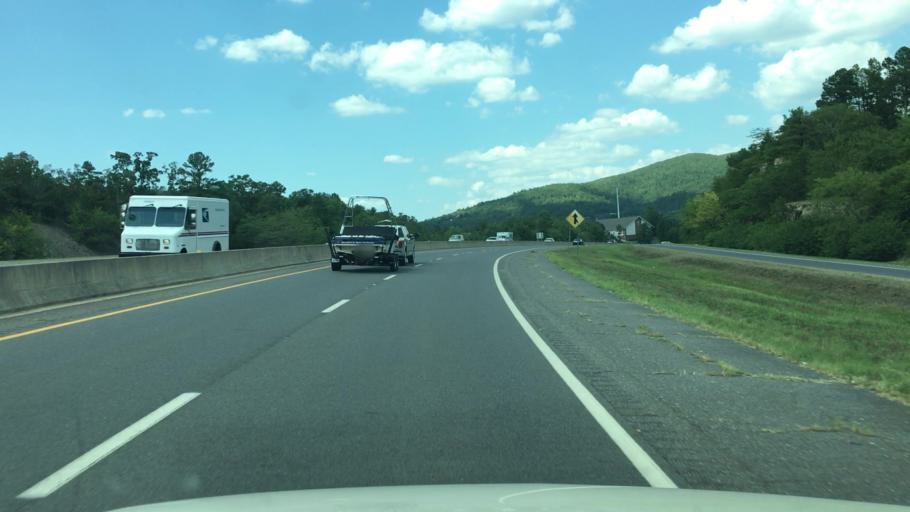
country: US
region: Arkansas
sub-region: Garland County
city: Rockwell
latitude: 34.4792
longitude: -93.1150
